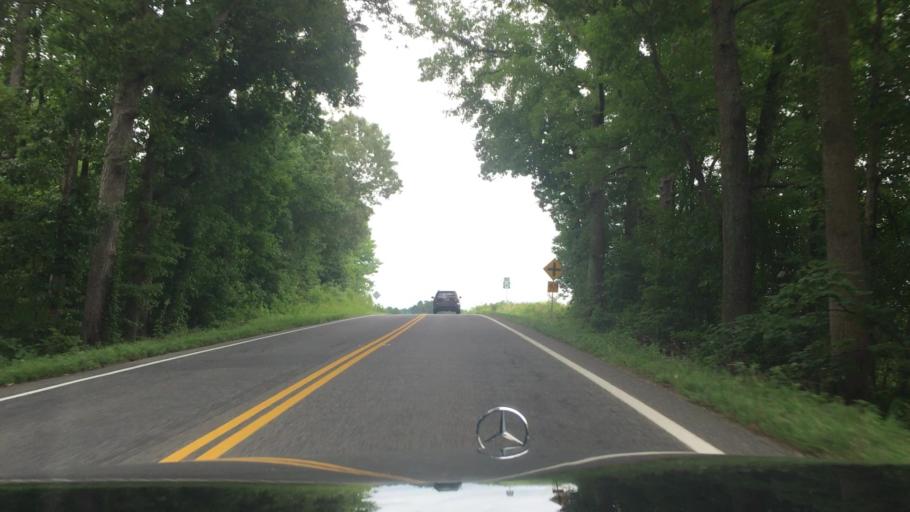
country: US
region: Virginia
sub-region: Nottoway County
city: Crewe
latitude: 37.2728
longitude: -78.1644
